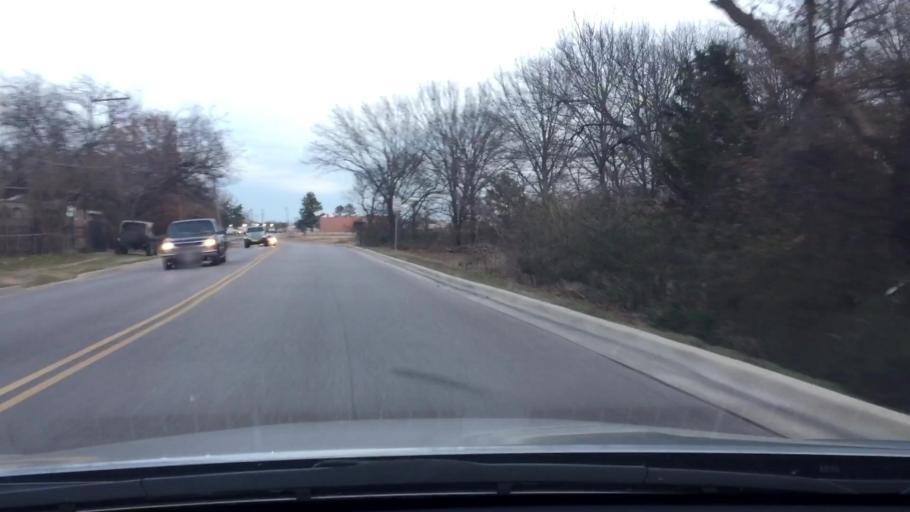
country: US
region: Oklahoma
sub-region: Carter County
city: Ardmore
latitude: 34.1801
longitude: -97.1505
